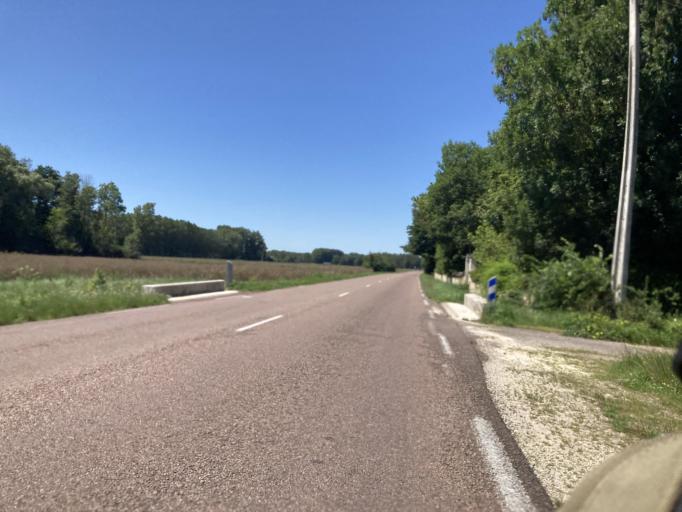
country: FR
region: Bourgogne
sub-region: Departement de l'Yonne
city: Laroche-Saint-Cydroine
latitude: 47.9642
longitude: 3.4780
